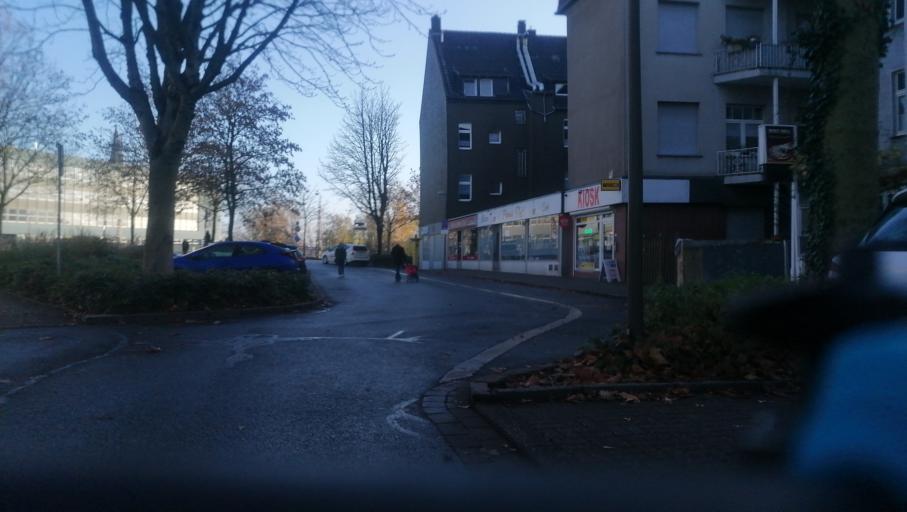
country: DE
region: North Rhine-Westphalia
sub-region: Regierungsbezirk Arnsberg
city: Dortmund
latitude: 51.4872
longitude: 7.4997
